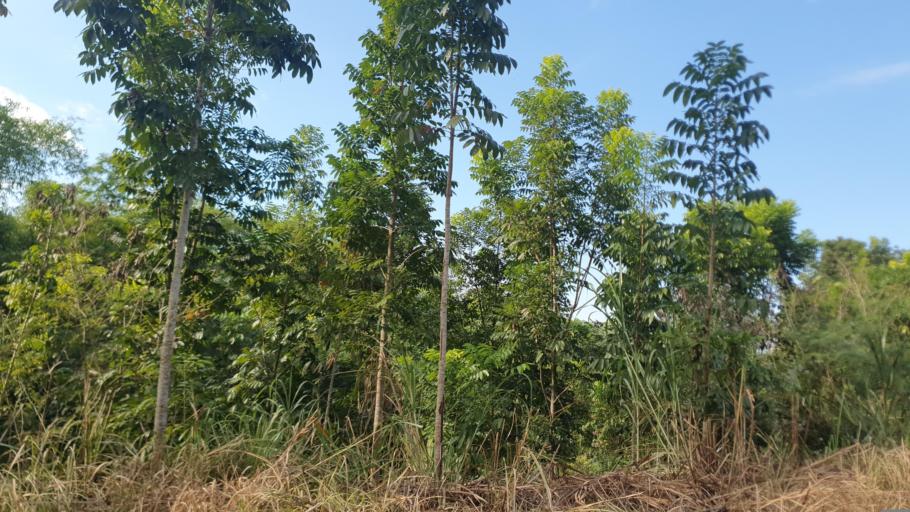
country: TW
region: Taiwan
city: Yujing
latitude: 23.0325
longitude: 120.3944
